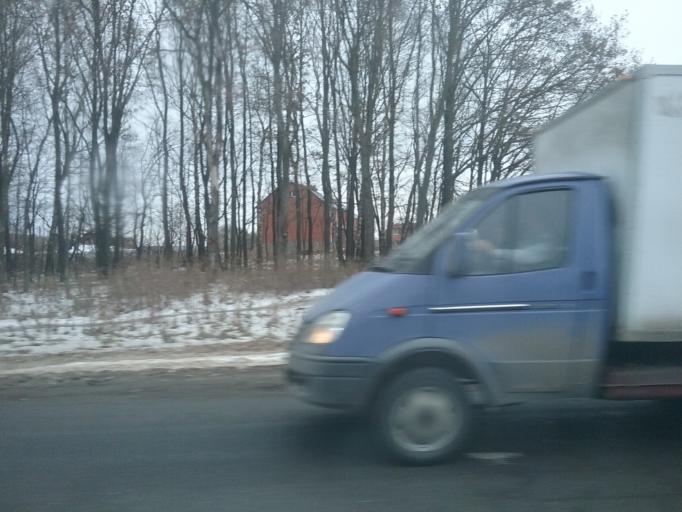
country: RU
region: Tula
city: Tula
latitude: 54.1601
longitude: 37.6368
